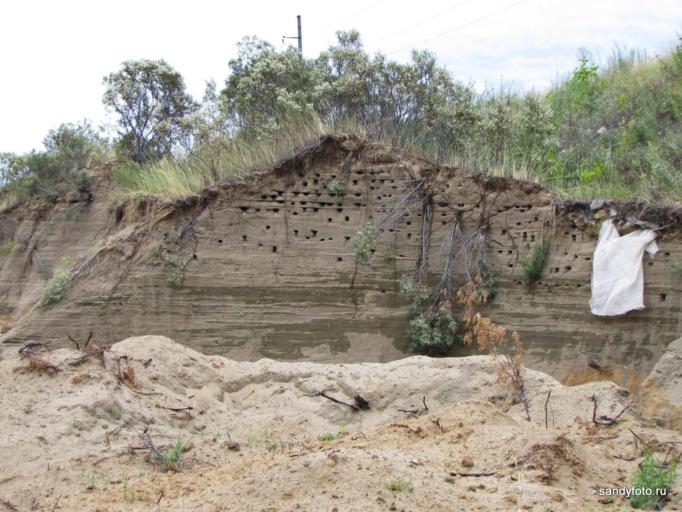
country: RU
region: Chelyabinsk
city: Troitsk
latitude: 54.0657
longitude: 61.5876
